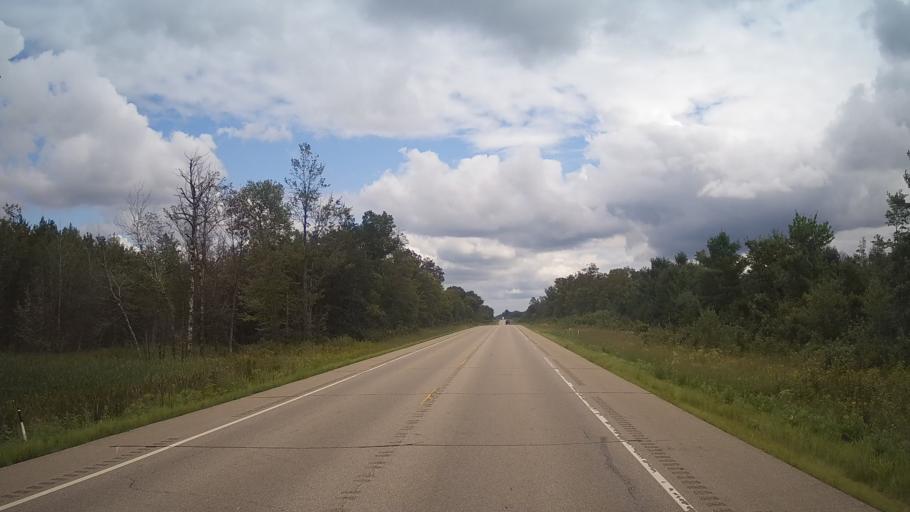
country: US
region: Wisconsin
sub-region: Adams County
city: Friendship
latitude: 44.0251
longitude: -89.7715
